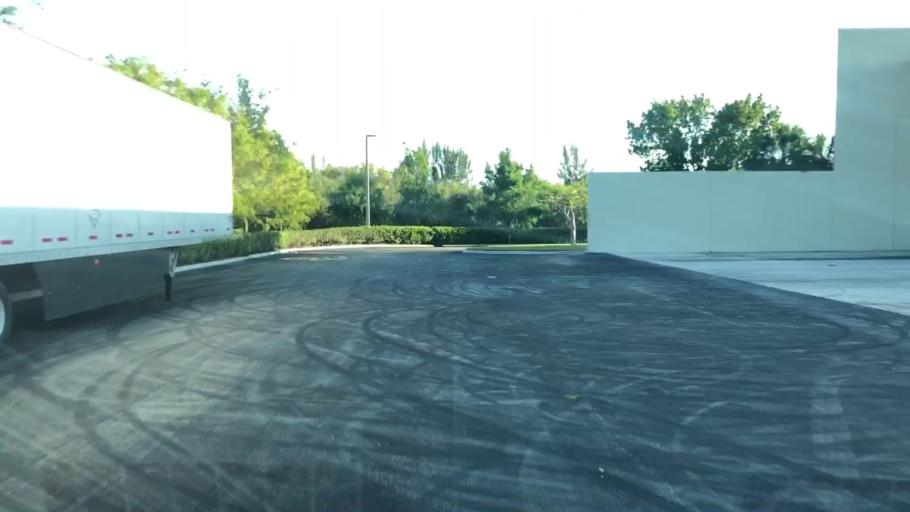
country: US
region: Florida
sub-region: Broward County
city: Tamarac
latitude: 26.1989
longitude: -80.2895
